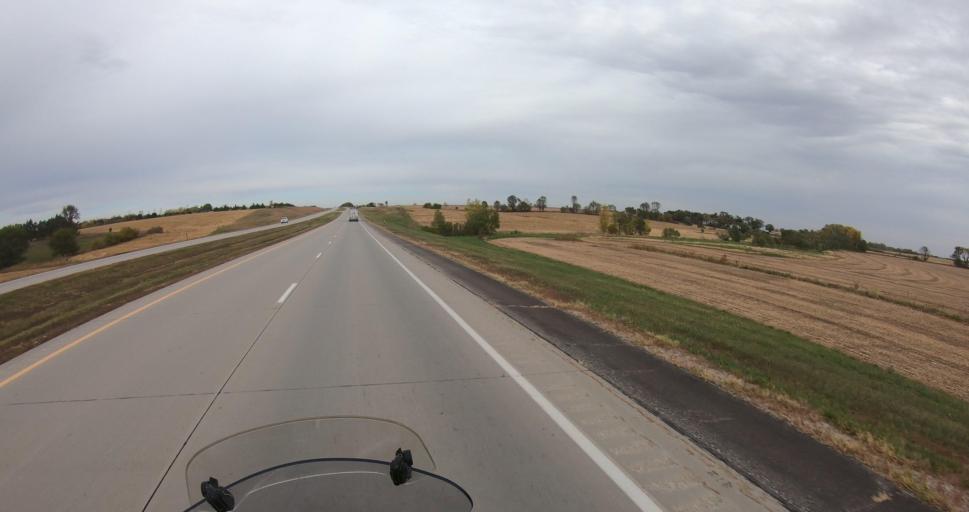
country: US
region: Nebraska
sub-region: Saunders County
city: Wahoo
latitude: 41.1625
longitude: -96.6297
